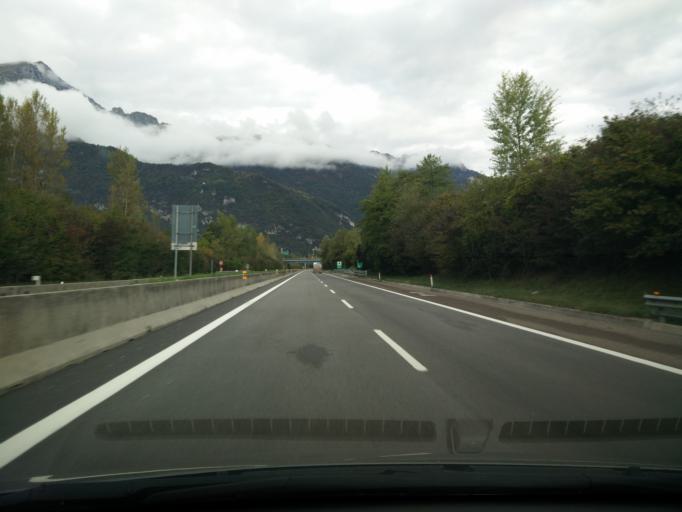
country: IT
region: Veneto
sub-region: Provincia di Belluno
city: Soccher-Paiane-Casan-Arsie
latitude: 46.1786
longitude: 12.2987
